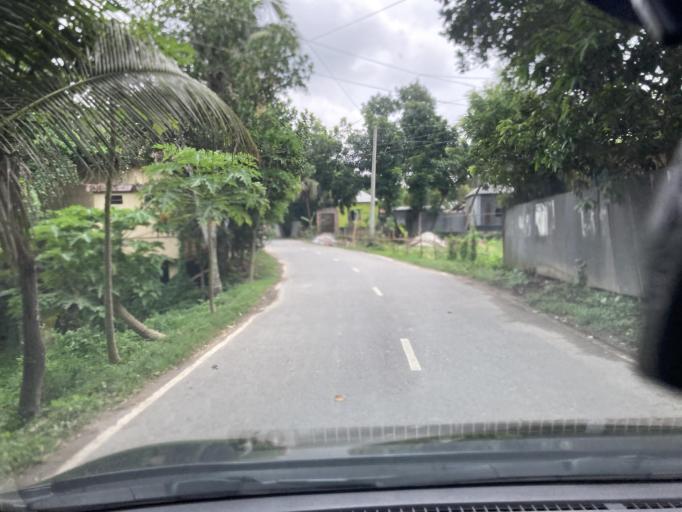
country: BD
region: Dhaka
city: Azimpur
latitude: 23.7870
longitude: 90.2169
